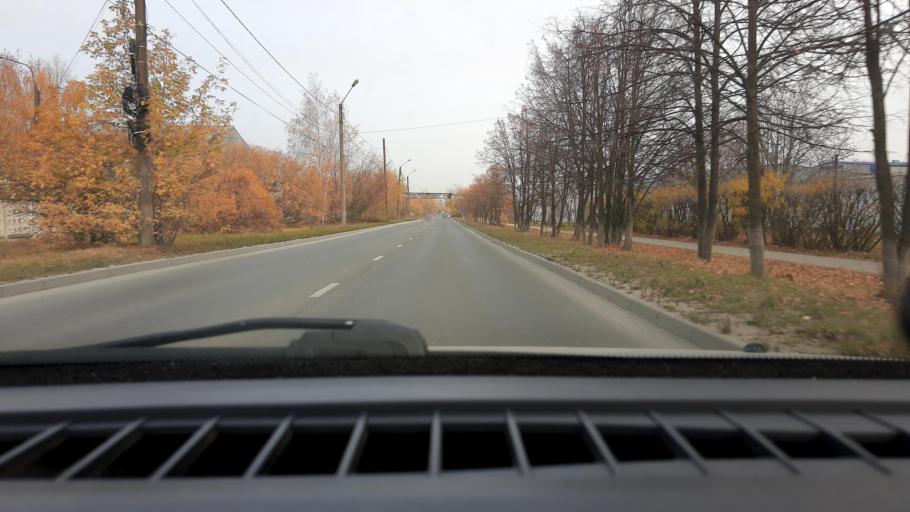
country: RU
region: Nizjnij Novgorod
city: Gorbatovka
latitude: 56.3503
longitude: 43.8072
